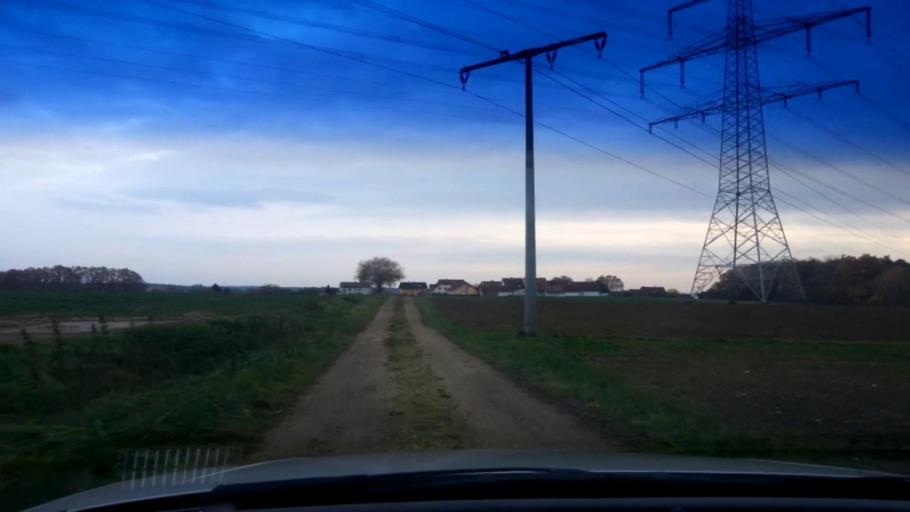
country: DE
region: Bavaria
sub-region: Upper Franconia
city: Memmelsdorf
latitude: 49.9464
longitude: 10.9529
